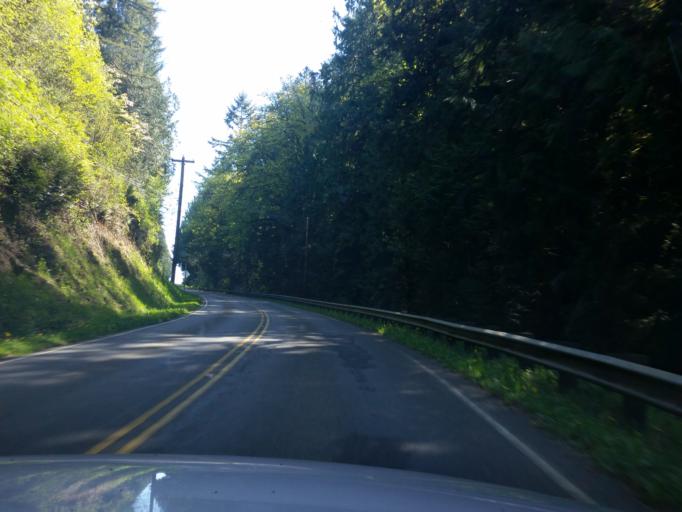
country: US
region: Washington
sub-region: Snohomish County
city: Three Lakes
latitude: 47.9633
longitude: -122.0174
